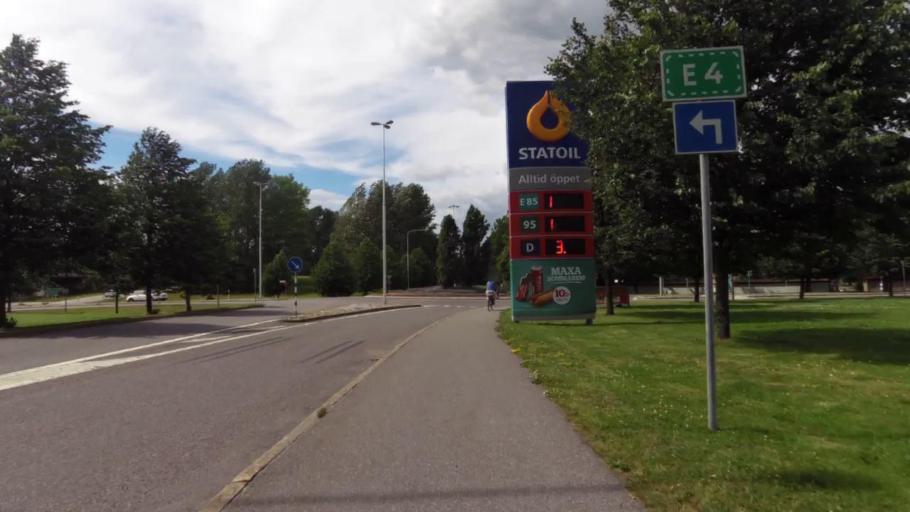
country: SE
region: OEstergoetland
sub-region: Linkopings Kommun
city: Malmslatt
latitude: 58.4055
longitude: 15.5594
